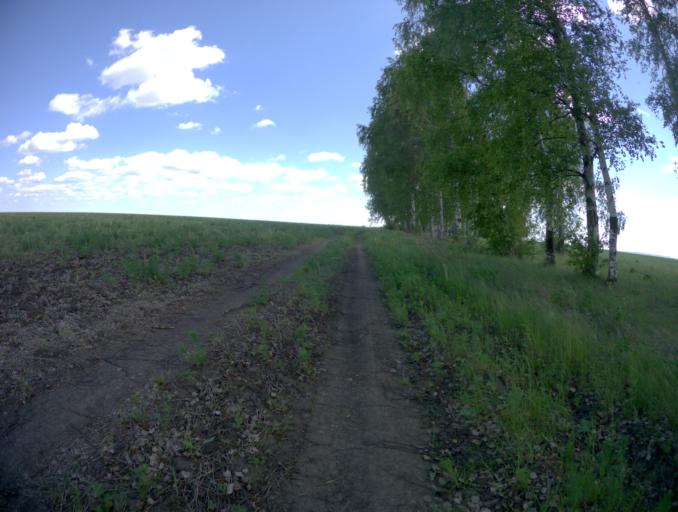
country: RU
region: Ivanovo
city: Gavrilov Posad
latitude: 56.4527
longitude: 40.2279
